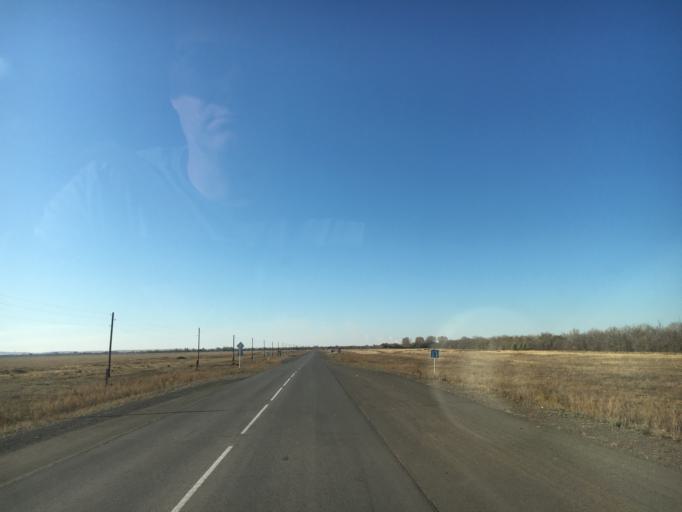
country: KZ
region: Qaraghandy
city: Tokarevka
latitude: 50.1203
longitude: 73.2100
